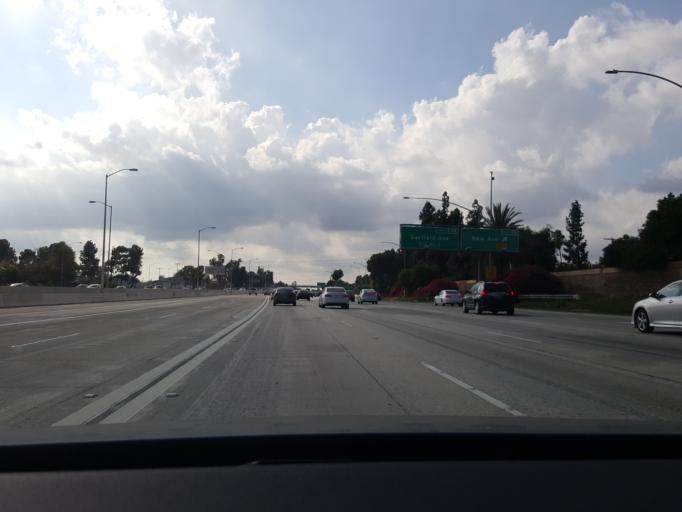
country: US
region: California
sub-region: Los Angeles County
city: South San Gabriel
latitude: 34.0721
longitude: -118.1052
